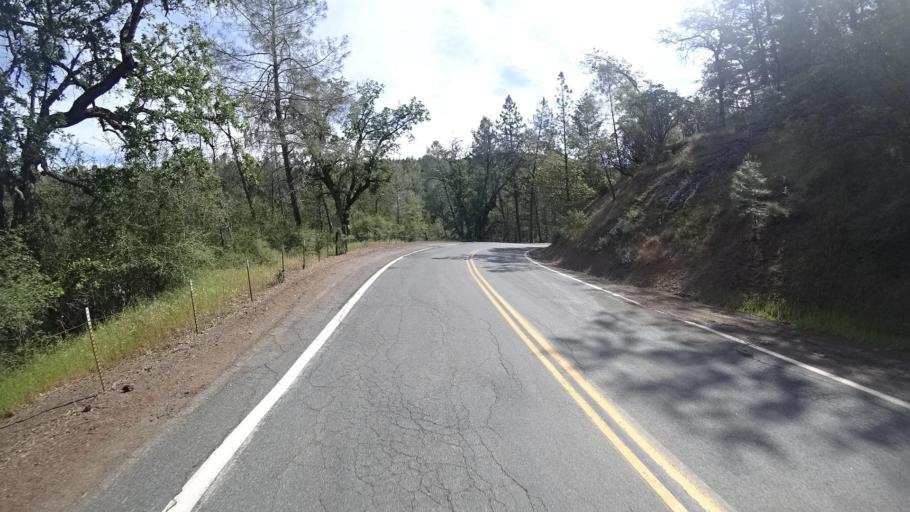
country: US
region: California
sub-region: Lake County
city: Cobb
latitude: 38.8584
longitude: -122.7446
